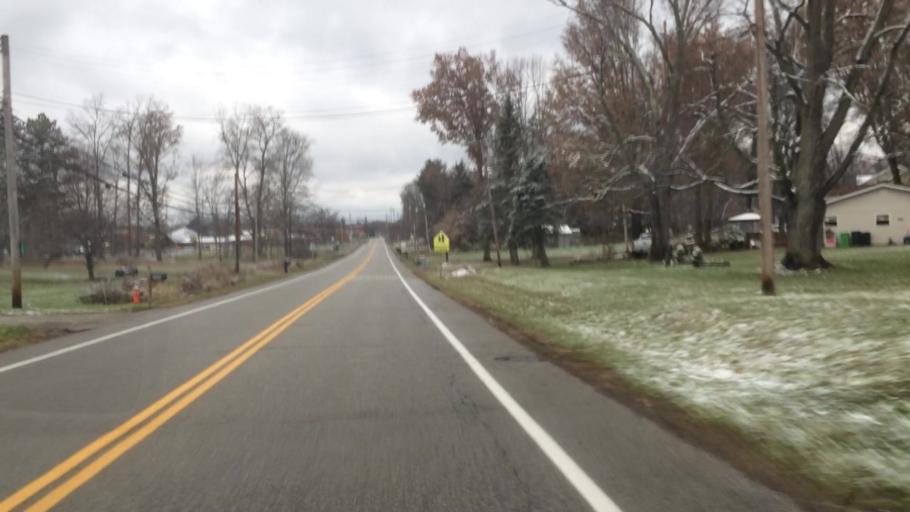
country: US
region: Ohio
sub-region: Summit County
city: Macedonia
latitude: 41.3083
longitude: -81.5341
